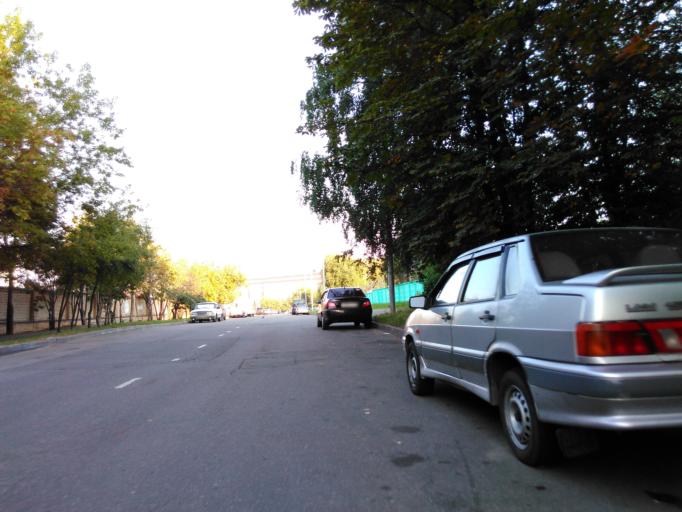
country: RU
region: Moskovskaya
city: Cheremushki
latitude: 55.6515
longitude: 37.5437
